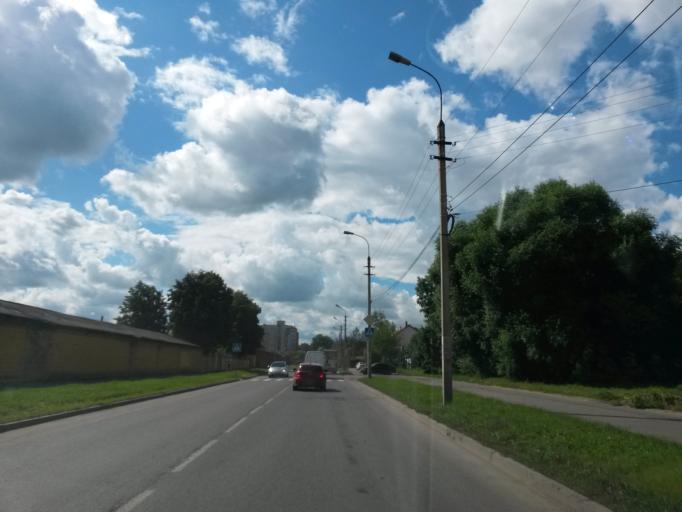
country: RU
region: Jaroslavl
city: Yaroslavl
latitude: 57.6088
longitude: 39.8736
